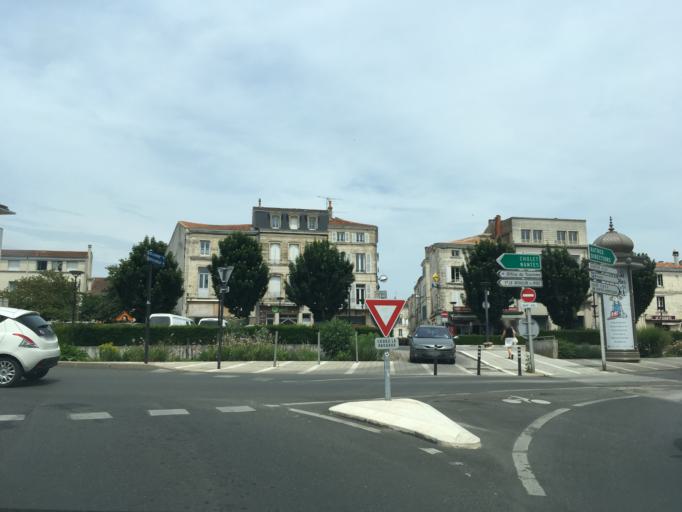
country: FR
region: Poitou-Charentes
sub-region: Departement des Deux-Sevres
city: Niort
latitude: 46.3212
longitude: -0.4654
